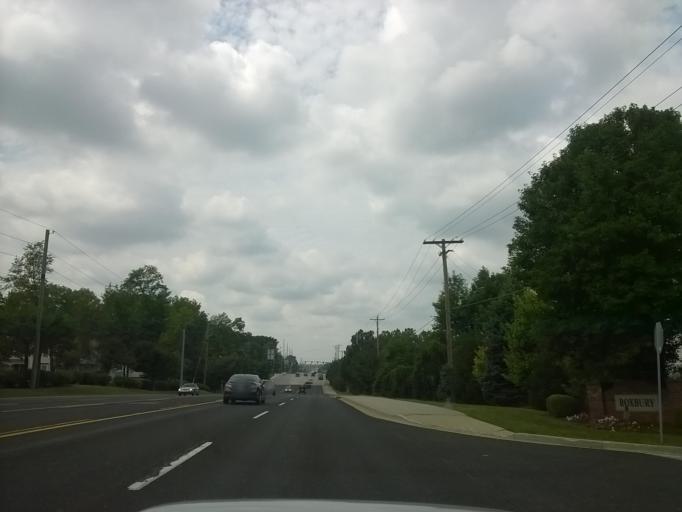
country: US
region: Indiana
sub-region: Hamilton County
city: Fishers
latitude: 39.9271
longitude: -86.0599
